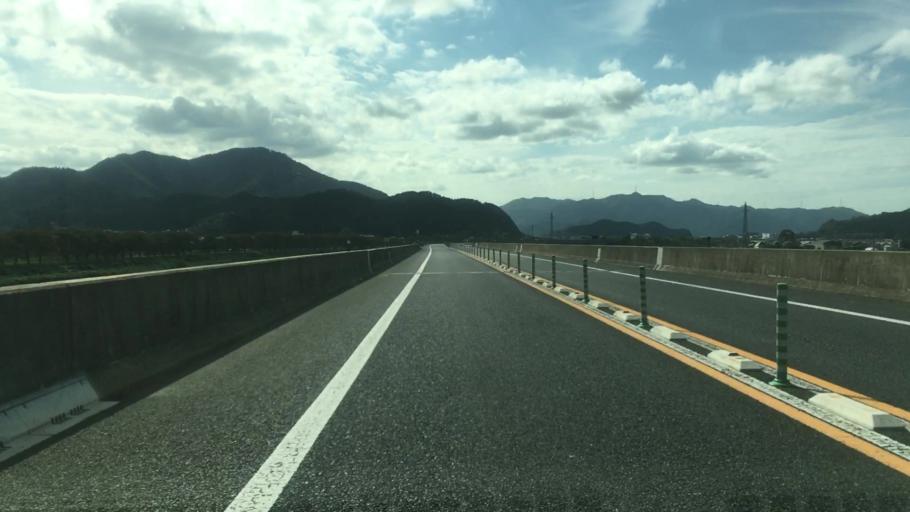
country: JP
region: Kyoto
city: Fukuchiyama
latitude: 35.1980
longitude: 135.0425
